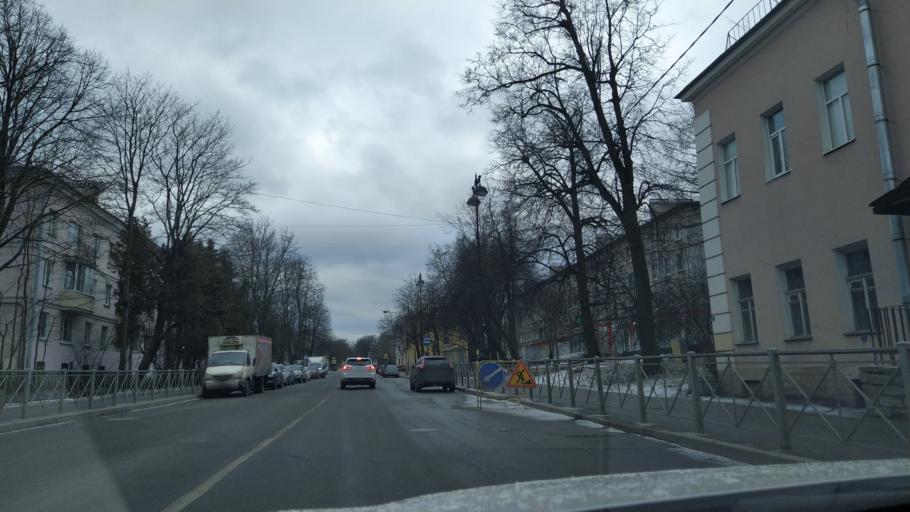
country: RU
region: St.-Petersburg
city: Pushkin
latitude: 59.7179
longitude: 30.4111
